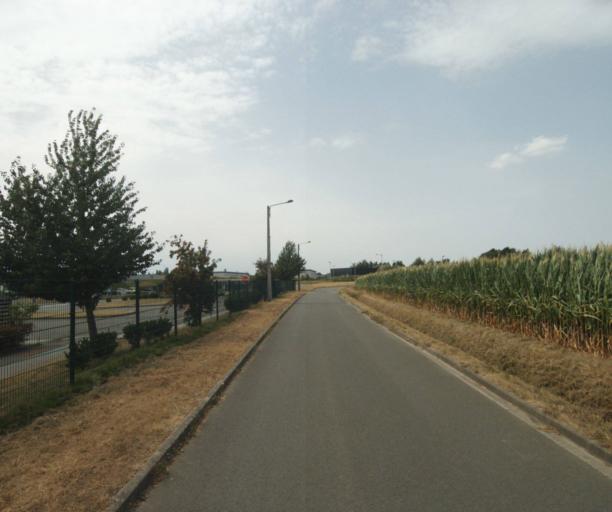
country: FR
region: Nord-Pas-de-Calais
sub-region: Departement du Nord
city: Leers
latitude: 50.6946
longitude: 3.2362
